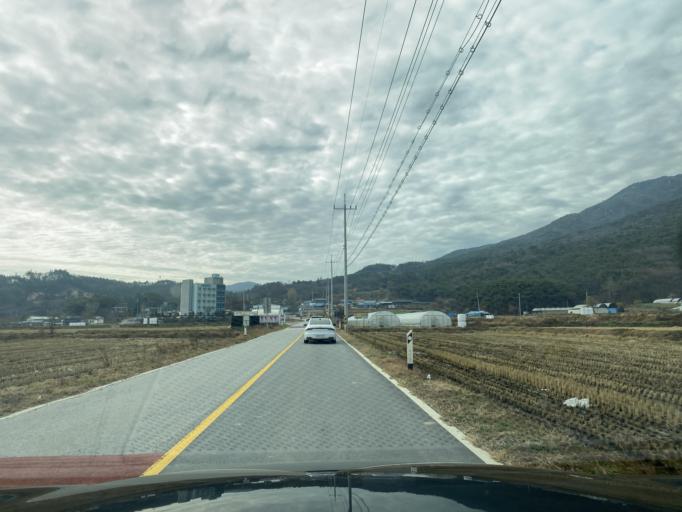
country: KR
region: Chungcheongnam-do
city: Hongsung
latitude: 36.6775
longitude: 126.6442
